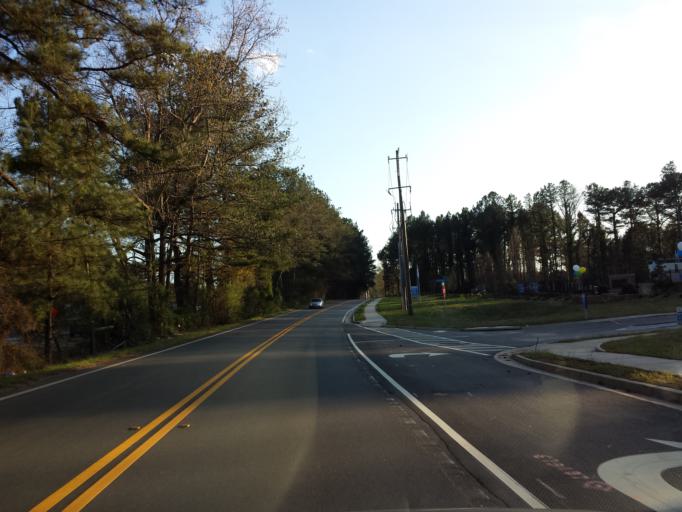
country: US
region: Georgia
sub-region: Cobb County
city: Vinings
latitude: 33.8794
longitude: -84.4738
